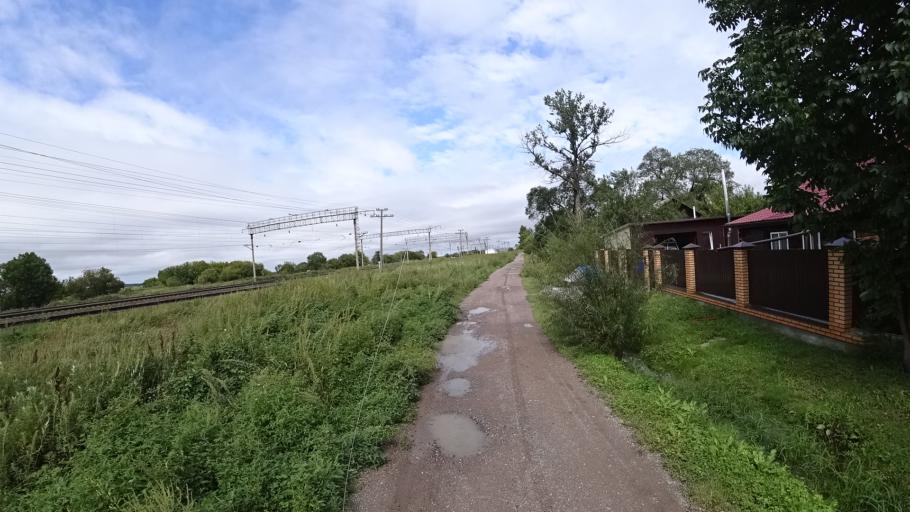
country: RU
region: Primorskiy
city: Lyalichi
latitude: 44.1360
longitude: 132.3728
